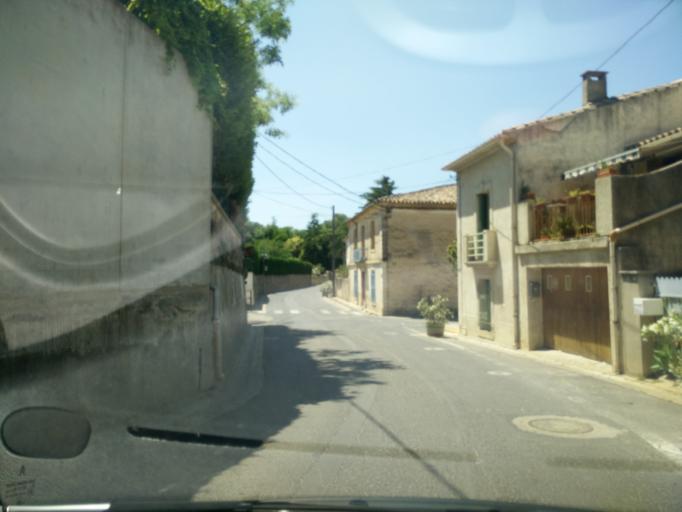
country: FR
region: Languedoc-Roussillon
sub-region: Departement de l'Herault
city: Saint-Christol
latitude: 43.7287
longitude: 4.0800
